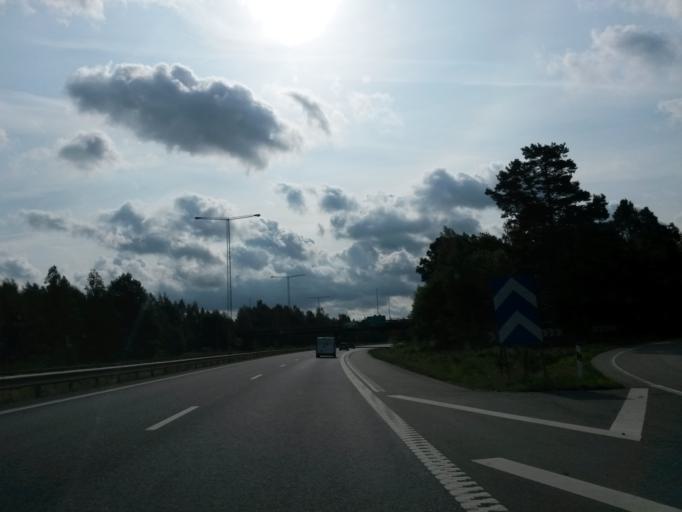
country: SE
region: Kronoberg
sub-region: Vaxjo Kommun
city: Vaexjoe
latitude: 56.8910
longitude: 14.7514
